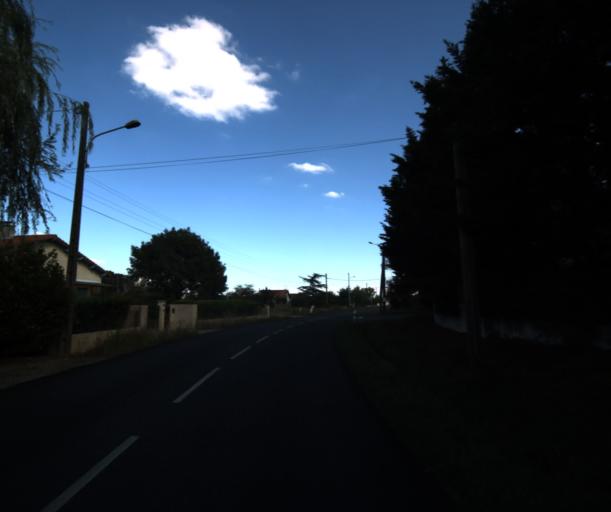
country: FR
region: Midi-Pyrenees
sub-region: Departement de la Haute-Garonne
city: Saint-Lys
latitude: 43.5023
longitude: 1.1925
